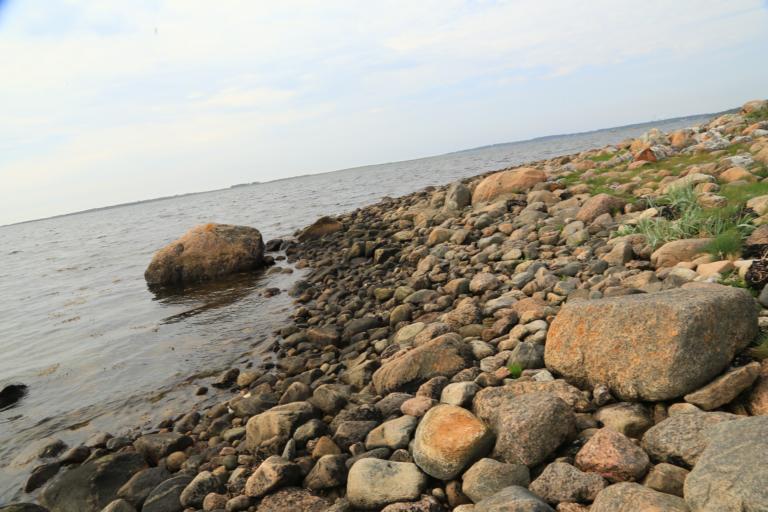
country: SE
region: Halland
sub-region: Varbergs Kommun
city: Varberg
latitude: 57.1529
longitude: 12.2107
